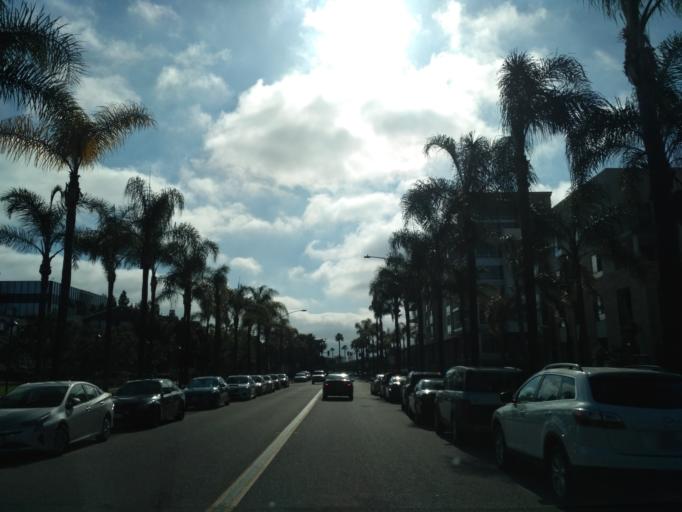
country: US
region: California
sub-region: San Diego County
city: San Diego
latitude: 32.8264
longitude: -117.1388
